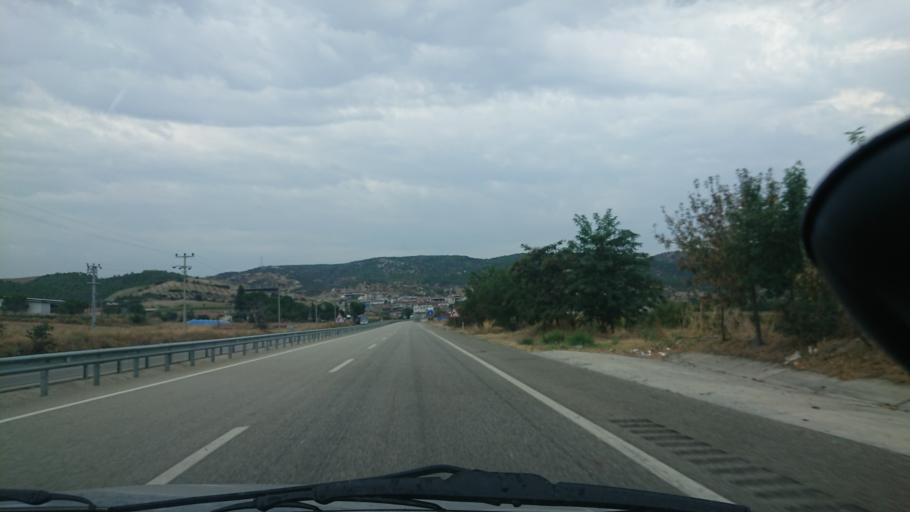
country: TR
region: Manisa
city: Selendi
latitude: 38.5971
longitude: 28.8121
